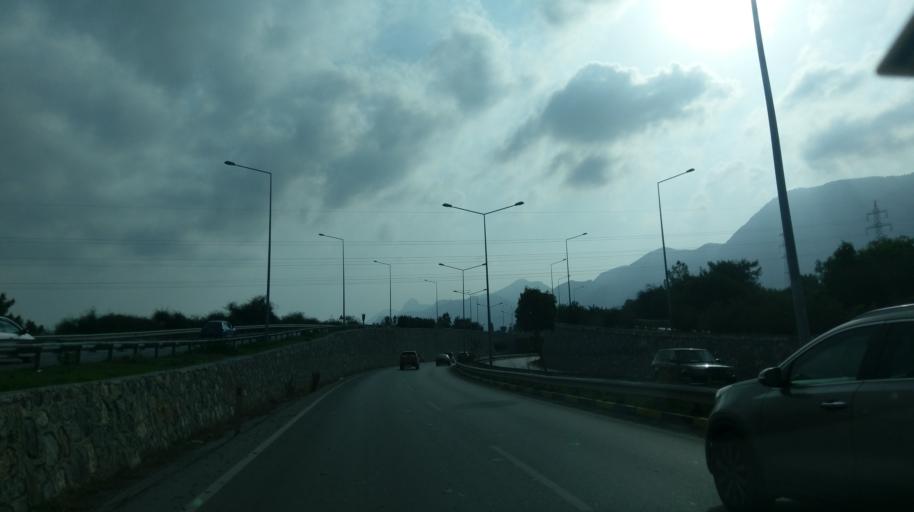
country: CY
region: Keryneia
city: Kyrenia
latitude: 35.3269
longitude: 33.3155
